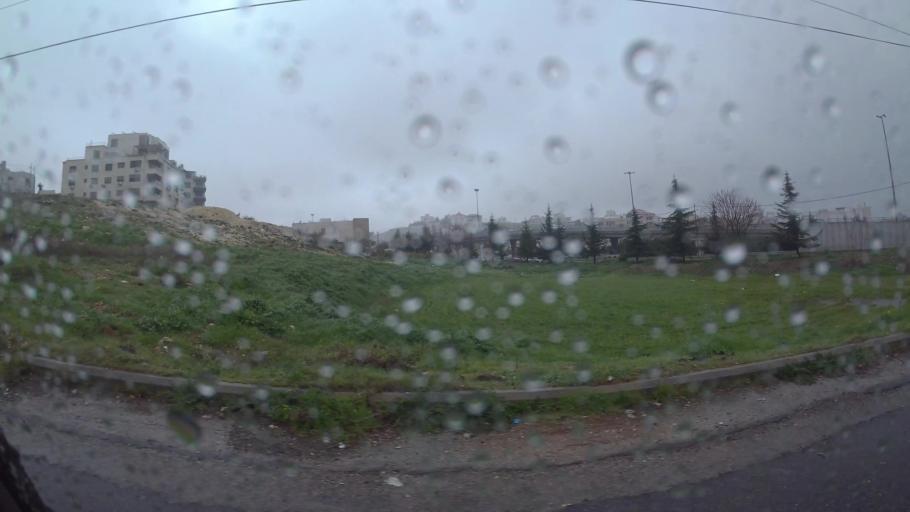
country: JO
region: Amman
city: Wadi as Sir
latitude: 31.9944
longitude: 35.8281
